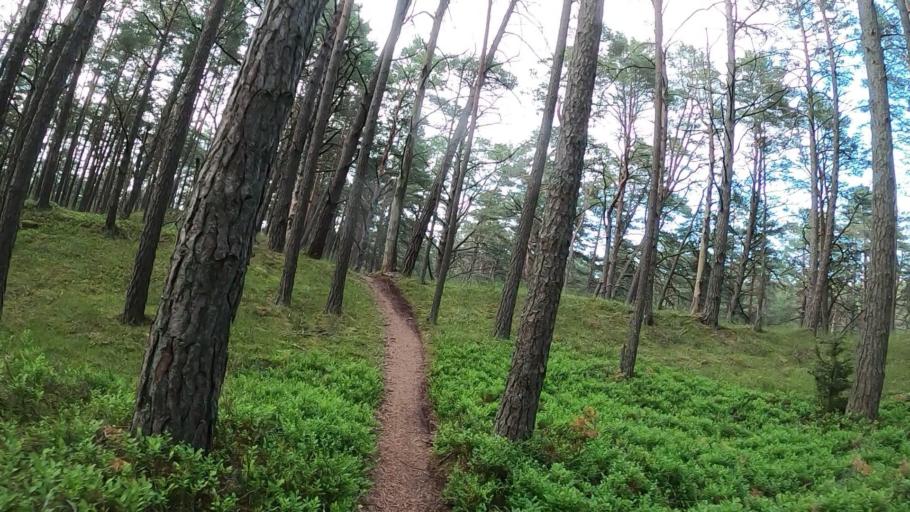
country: LV
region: Carnikava
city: Carnikava
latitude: 57.1249
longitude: 24.2168
